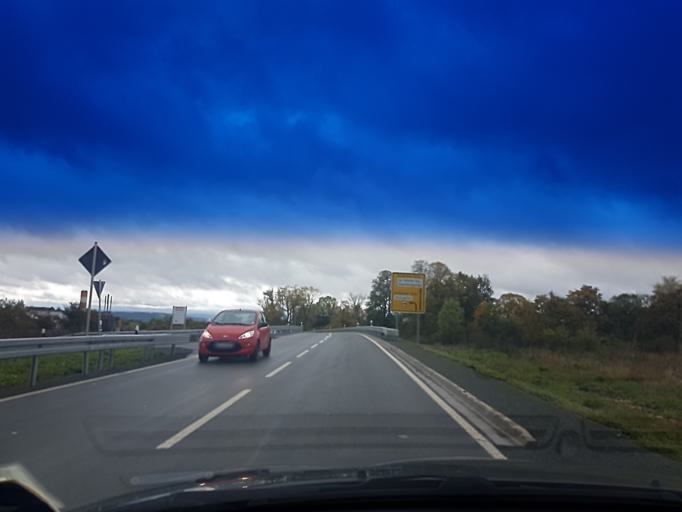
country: DE
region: Bavaria
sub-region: Upper Franconia
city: Bindlach
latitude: 49.9960
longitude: 11.6232
